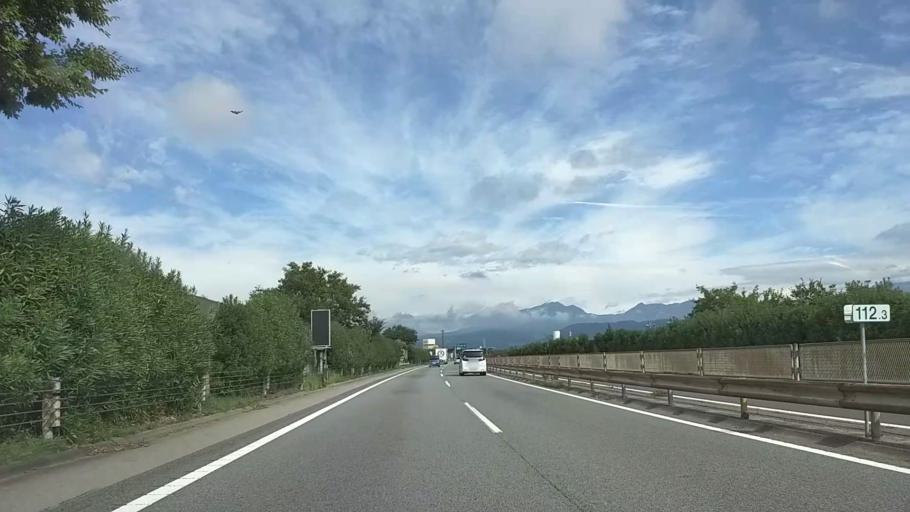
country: JP
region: Yamanashi
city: Kofu-shi
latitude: 35.6354
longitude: 138.5389
